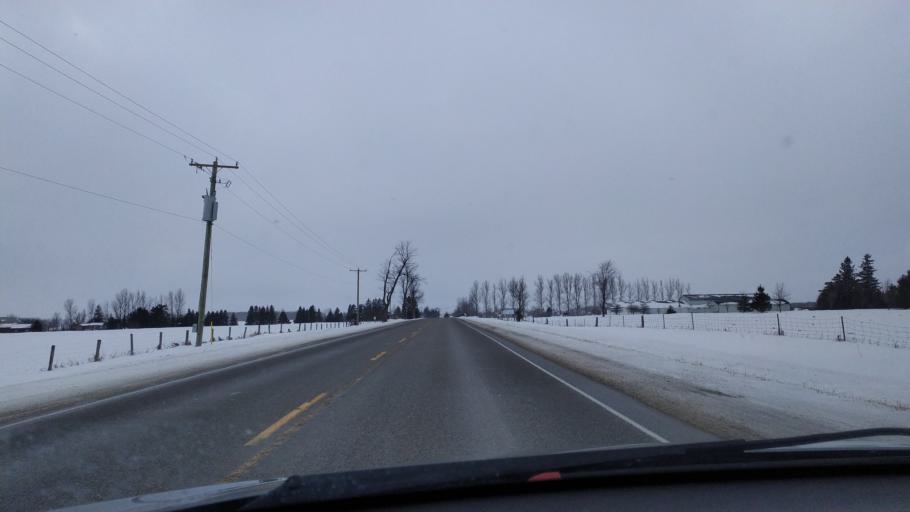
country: CA
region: Ontario
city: North Perth
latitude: 43.5938
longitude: -80.8880
